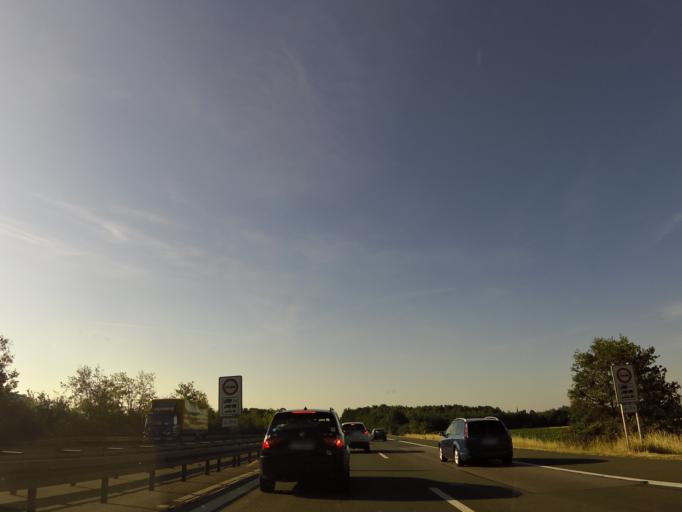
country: DE
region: Bavaria
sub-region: Regierungsbezirk Mittelfranken
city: Hessdorf
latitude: 49.6547
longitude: 10.8975
